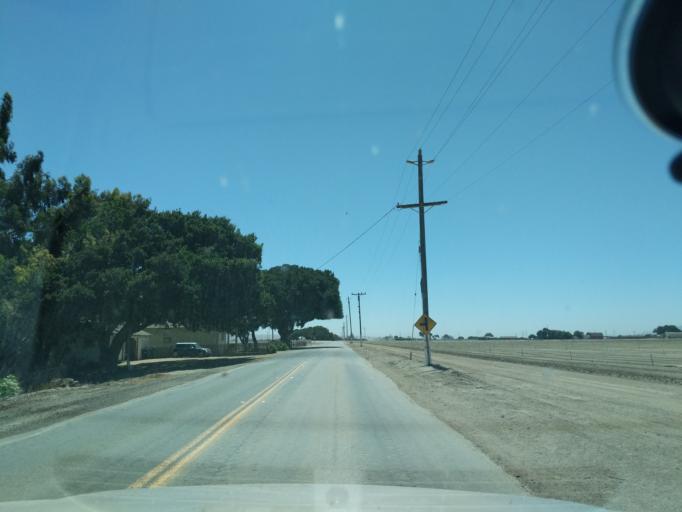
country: US
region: California
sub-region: Monterey County
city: Soledad
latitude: 36.4052
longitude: -121.3519
